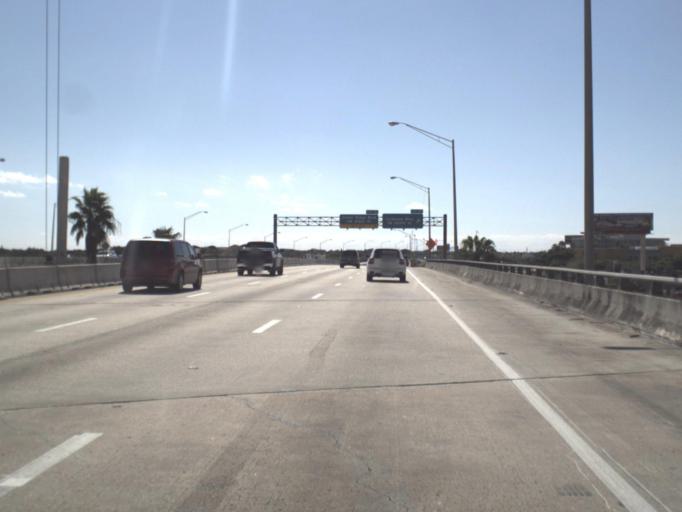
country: US
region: Florida
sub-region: Miami-Dade County
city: Cutler Ridge
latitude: 25.5828
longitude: -80.3667
